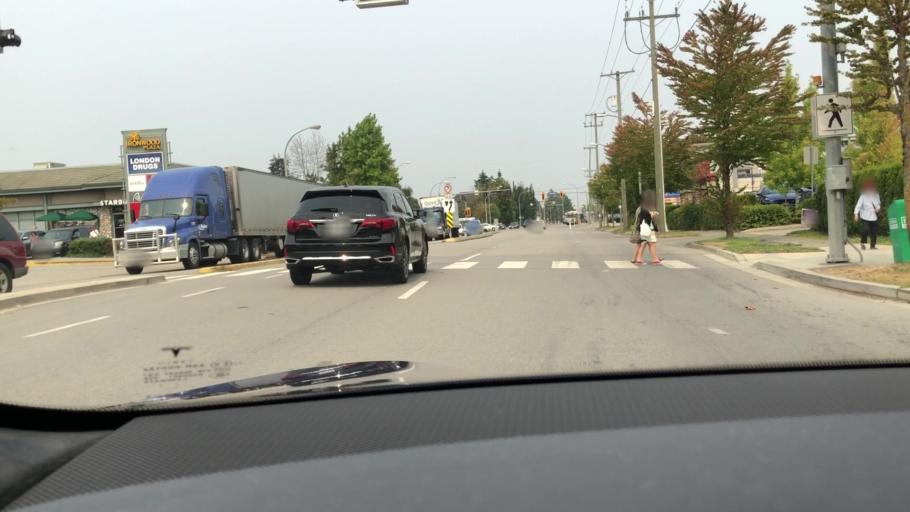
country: CA
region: British Columbia
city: Ladner
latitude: 49.1319
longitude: -123.0920
